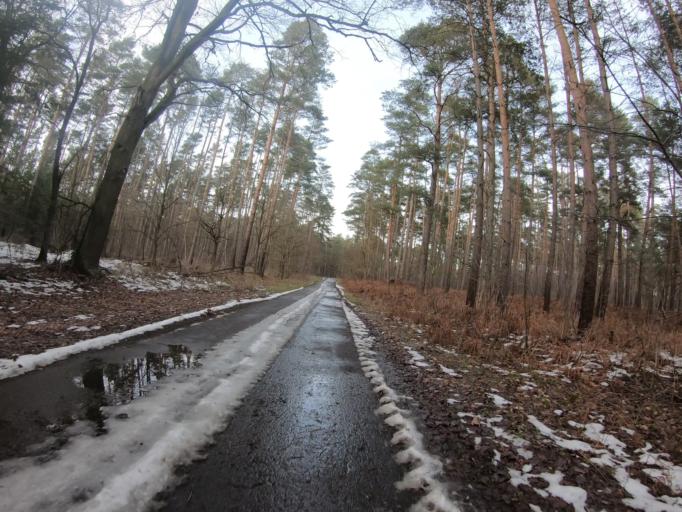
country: DE
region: Lower Saxony
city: Wagenhoff
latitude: 52.5026
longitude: 10.4624
